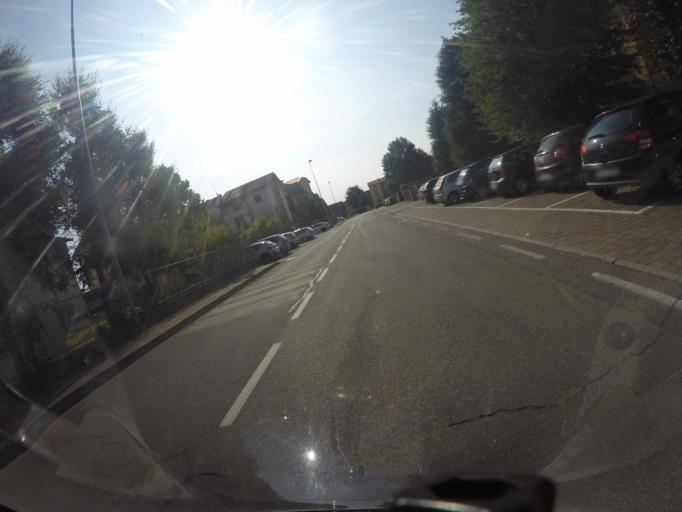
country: IT
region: Lombardy
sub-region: Provincia di Monza e Brianza
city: Aicurzio
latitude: 45.6363
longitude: 9.4214
